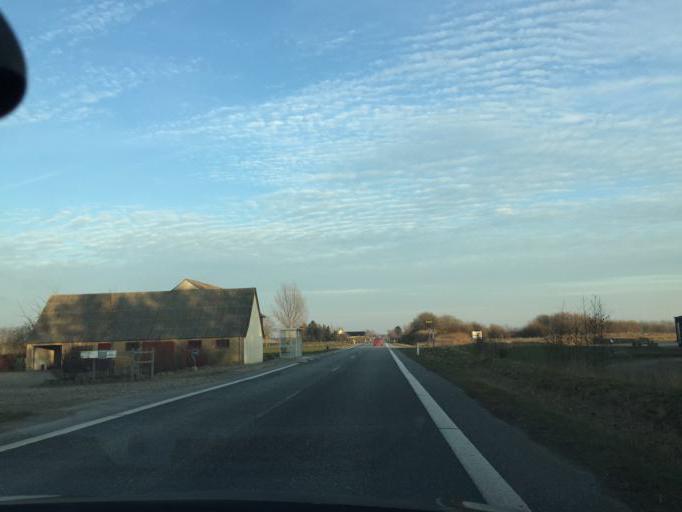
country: DK
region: South Denmark
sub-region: Faaborg-Midtfyn Kommune
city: Arslev
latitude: 55.3329
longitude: 10.5215
